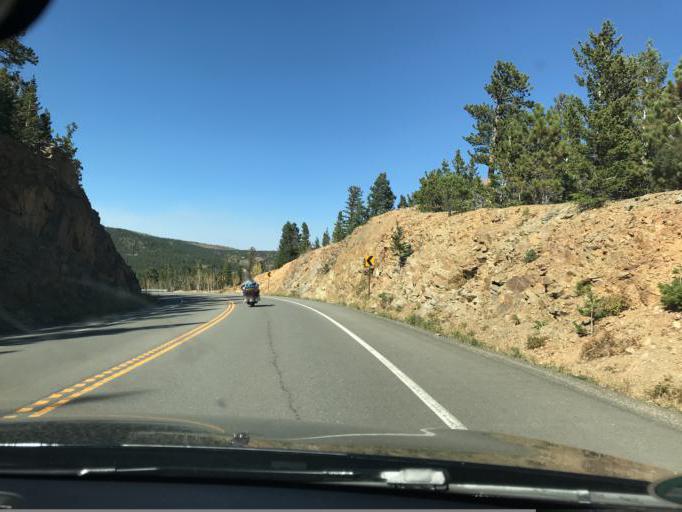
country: US
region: Colorado
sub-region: Boulder County
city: Nederland
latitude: 40.0501
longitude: -105.5151
